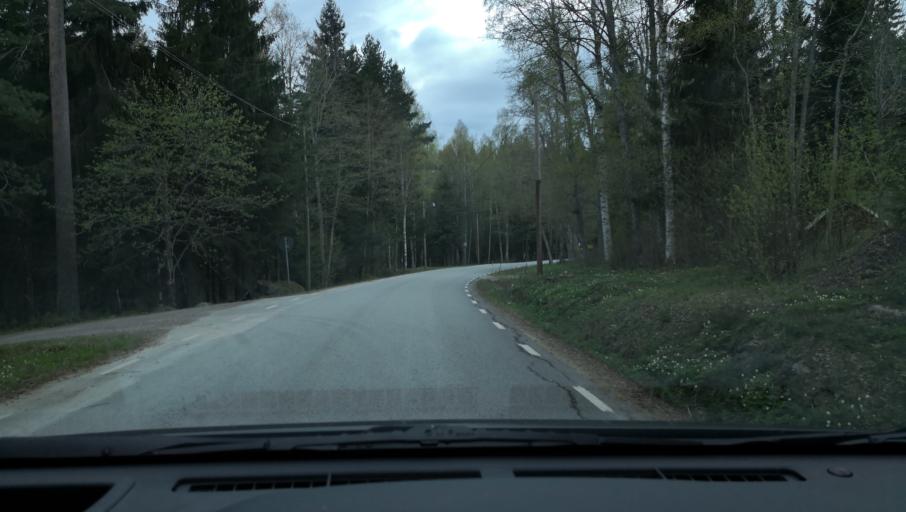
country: SE
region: Vaestmanland
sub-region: Norbergs Kommun
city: Norberg
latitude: 60.0891
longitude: 15.8758
